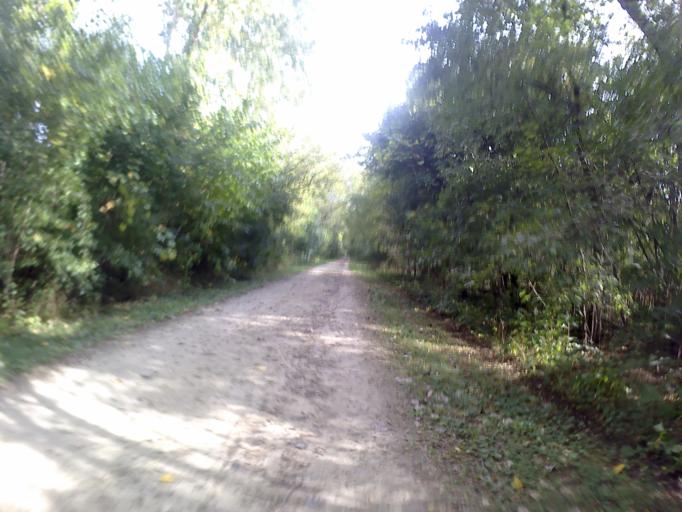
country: US
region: Illinois
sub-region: DuPage County
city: Winfield
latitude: 41.8863
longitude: -88.1479
